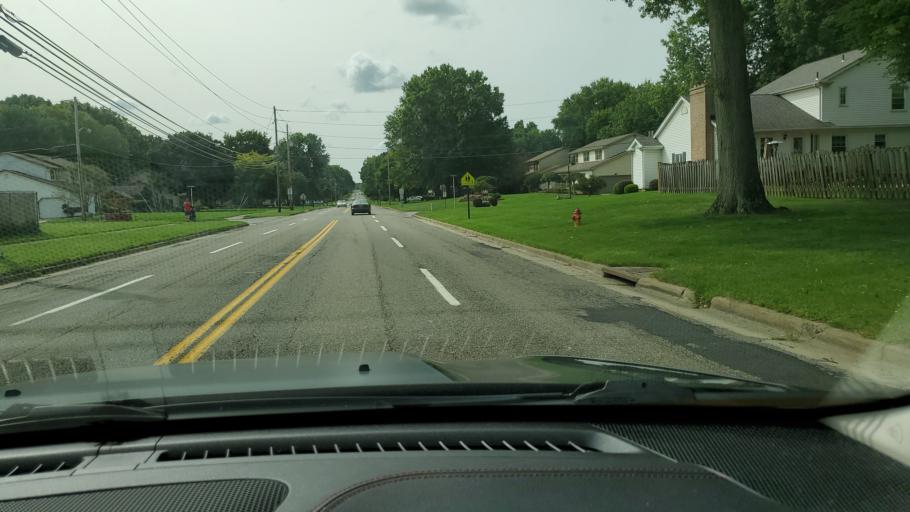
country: US
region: Ohio
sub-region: Mahoning County
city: Boardman
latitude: 41.0098
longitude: -80.6723
